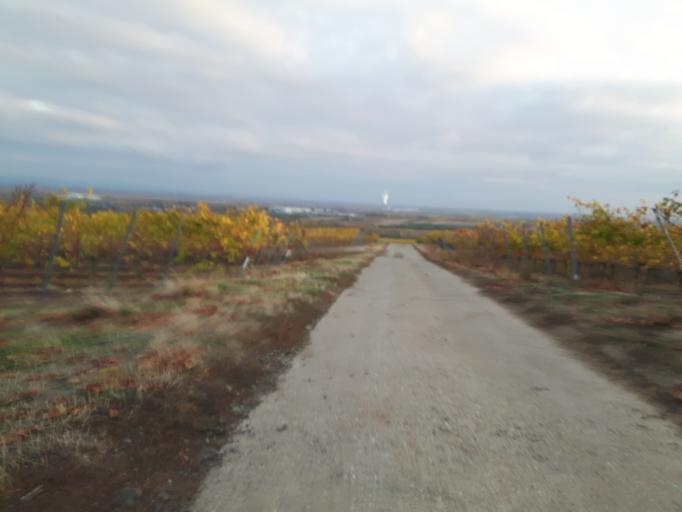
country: DE
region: Rheinland-Pfalz
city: Molsheim
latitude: 49.6496
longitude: 8.1822
